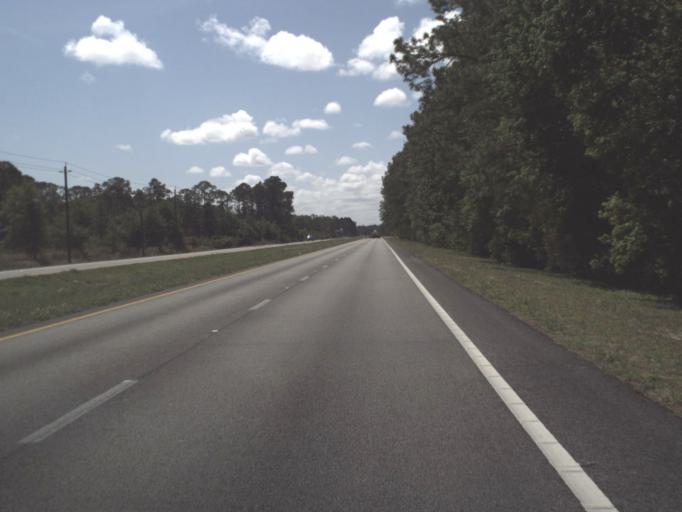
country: US
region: Florida
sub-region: Flagler County
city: Bunnell
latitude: 29.4000
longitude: -81.1940
